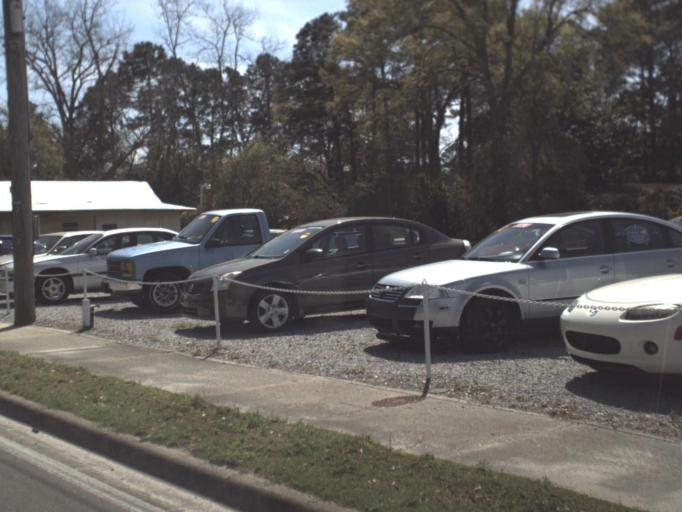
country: US
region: Florida
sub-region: Bay County
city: Lynn Haven
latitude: 30.2401
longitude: -85.6488
